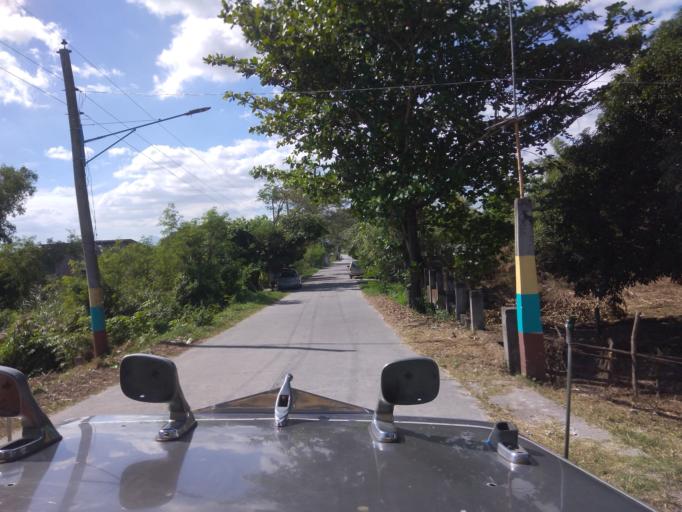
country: PH
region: Central Luzon
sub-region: Province of Pampanga
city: Santa Rita
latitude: 15.0300
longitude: 120.6290
